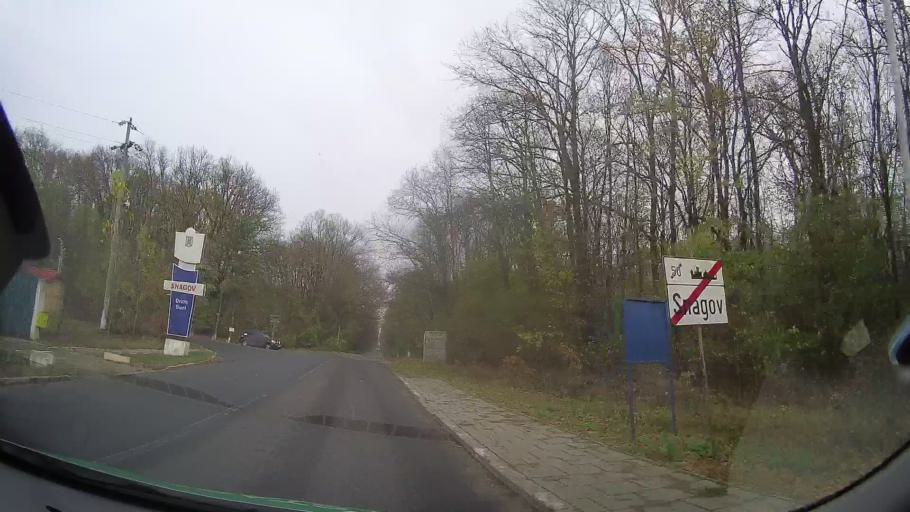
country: RO
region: Ilfov
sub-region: Comuna Snagov
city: Snagov
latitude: 44.7139
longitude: 26.1928
